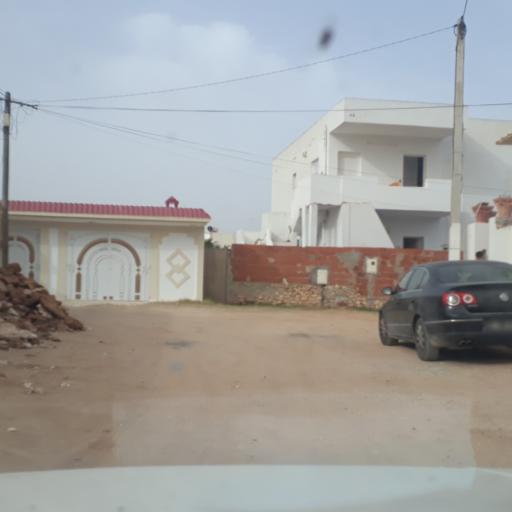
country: TN
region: Safaqis
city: Al Qarmadah
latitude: 34.8221
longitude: 10.7787
